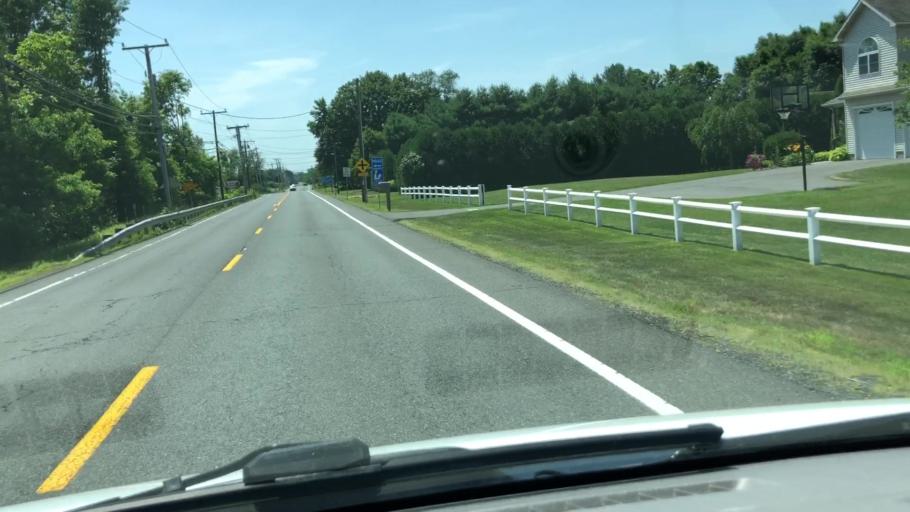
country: US
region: Massachusetts
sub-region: Franklin County
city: Whately
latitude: 42.4467
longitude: -72.6263
